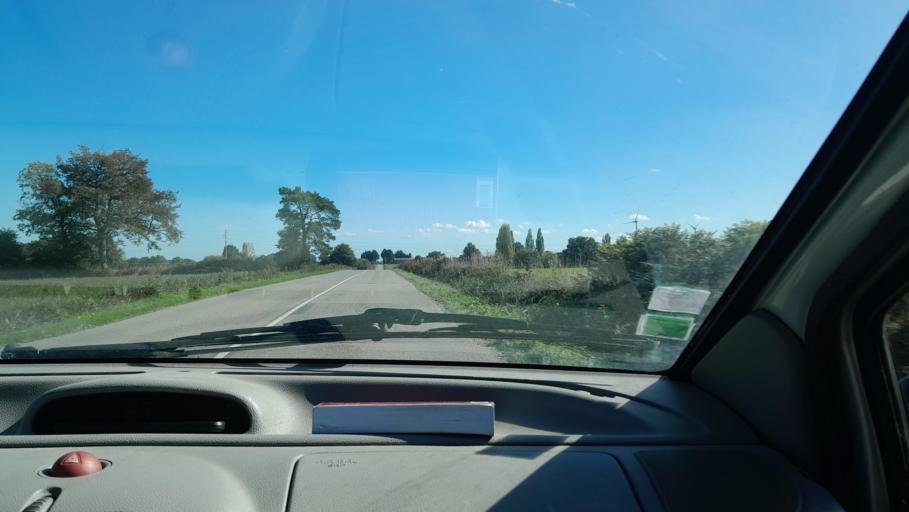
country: FR
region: Pays de la Loire
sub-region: Departement de la Mayenne
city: Quelaines-Saint-Gault
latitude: 47.9340
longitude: -0.8469
